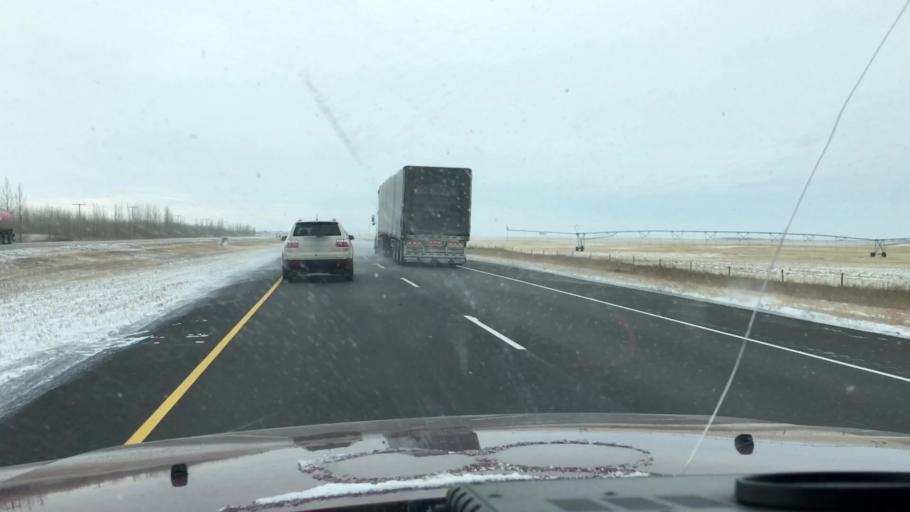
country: CA
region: Saskatchewan
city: Saskatoon
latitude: 51.7740
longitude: -106.4763
